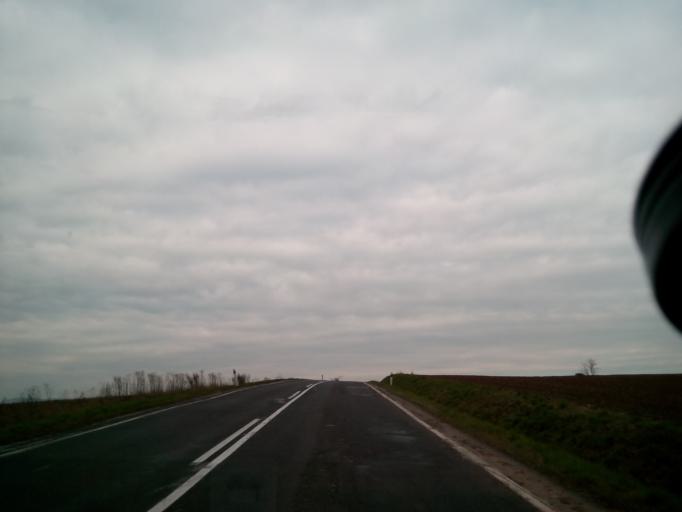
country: SK
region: Presovsky
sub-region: Okres Presov
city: Presov
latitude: 49.0809
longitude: 21.3181
